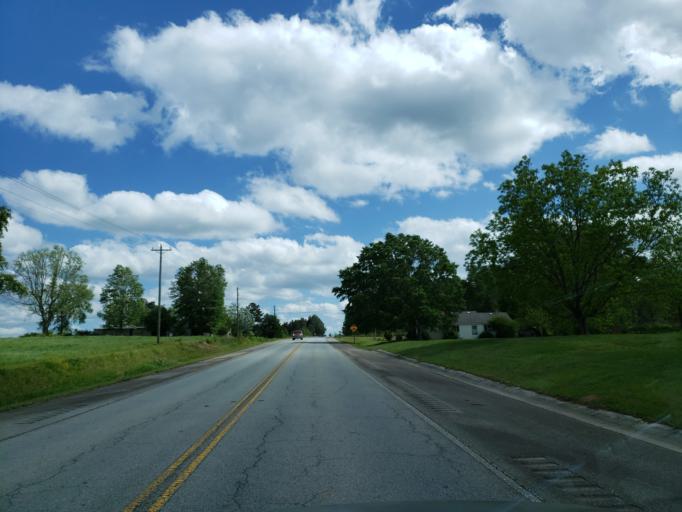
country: US
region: Georgia
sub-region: Haralson County
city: Bremen
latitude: 33.7341
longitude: -85.1127
